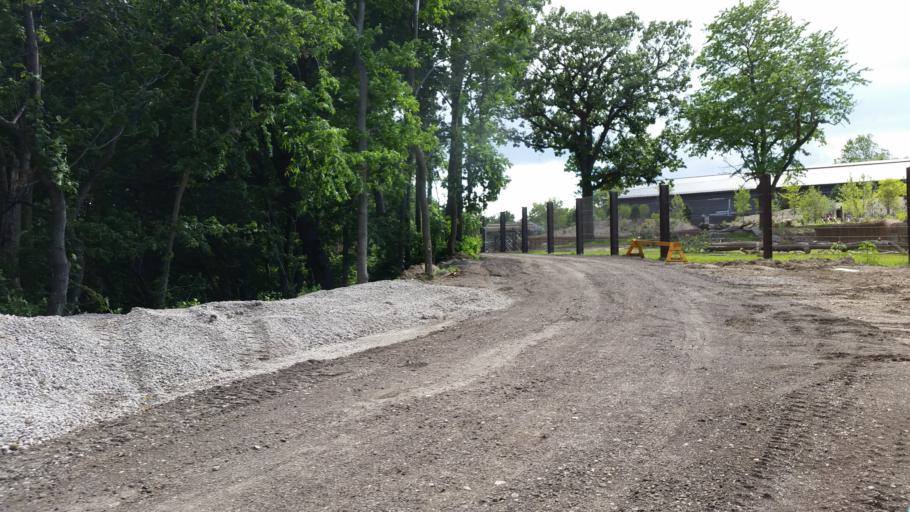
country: US
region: Nebraska
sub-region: Douglas County
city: Omaha
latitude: 41.2227
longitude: -95.9255
